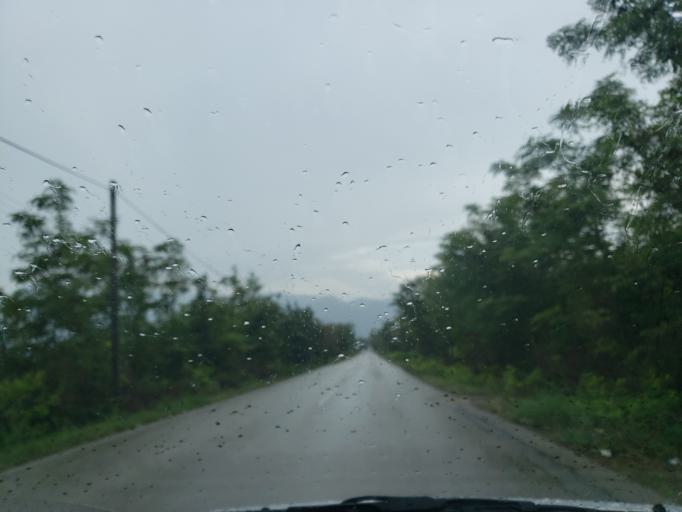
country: GR
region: Central Greece
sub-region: Nomos Fthiotidos
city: Anthili
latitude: 38.8327
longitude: 22.4414
